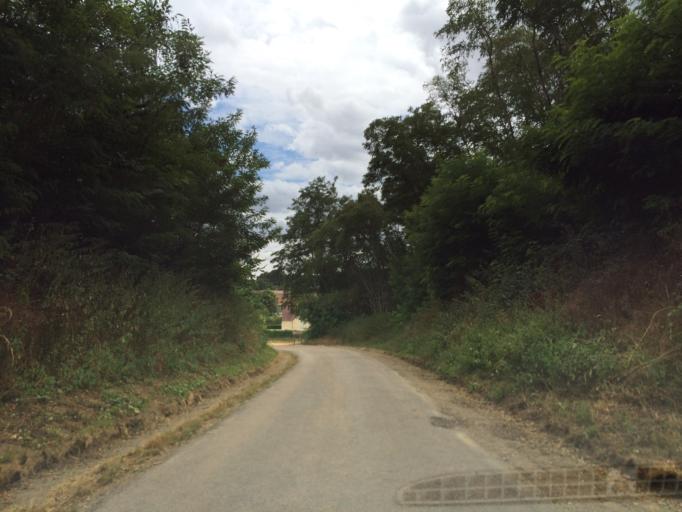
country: FR
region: Bourgogne
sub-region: Departement de l'Yonne
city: Fleury-la-Vallee
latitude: 47.8493
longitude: 3.4042
